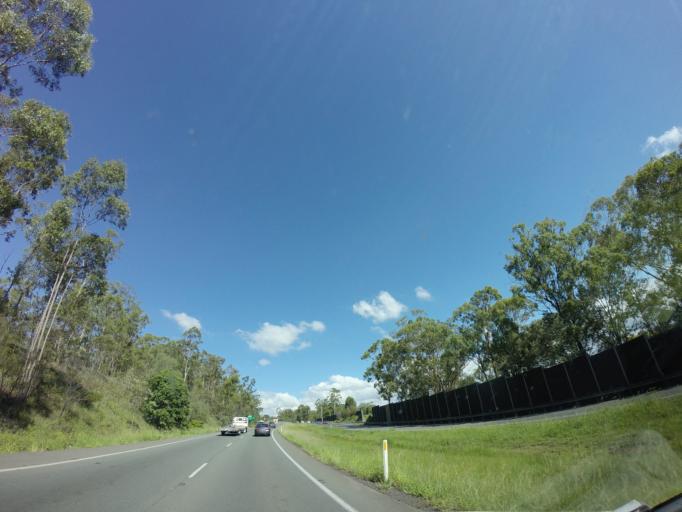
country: AU
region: Queensland
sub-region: Ipswich
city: Brassall
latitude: -27.5794
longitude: 152.7480
